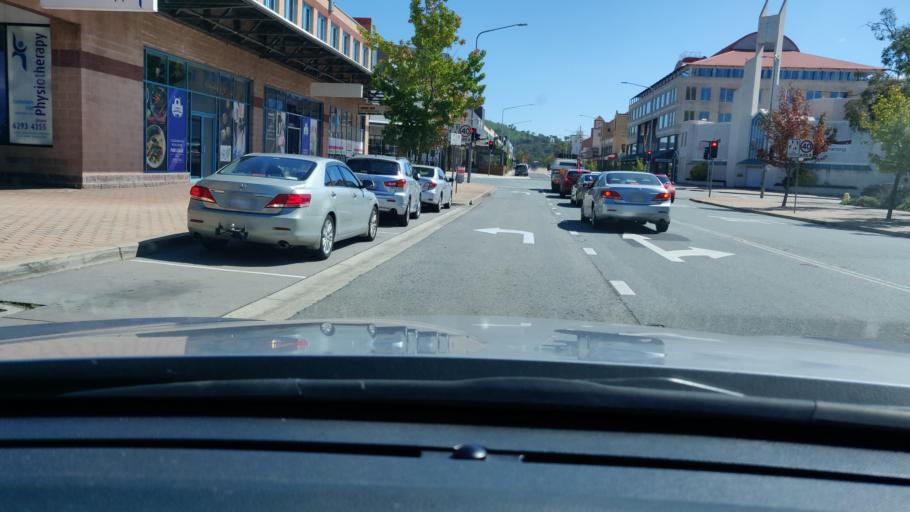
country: AU
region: Australian Capital Territory
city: Macarthur
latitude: -35.4175
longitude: 149.0689
